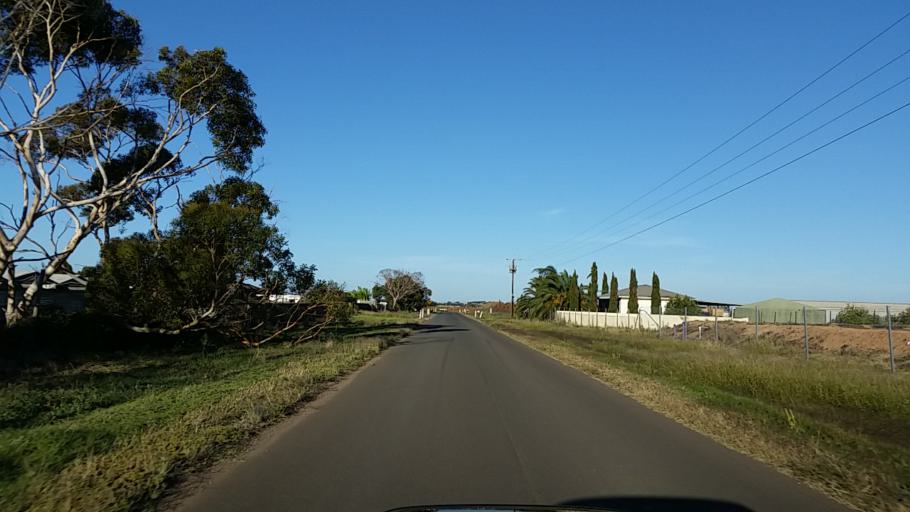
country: AU
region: South Australia
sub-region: Playford
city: Virginia
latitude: -34.6716
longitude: 138.5326
